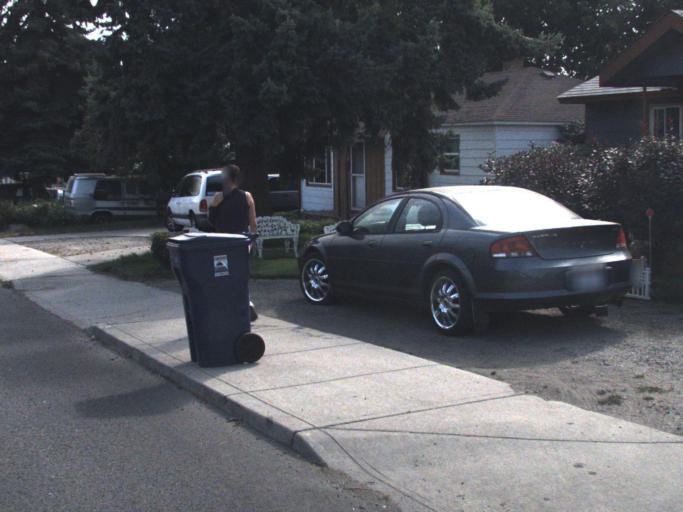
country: US
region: Washington
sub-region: Spokane County
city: Town and Country
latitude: 47.7154
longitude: -117.4462
